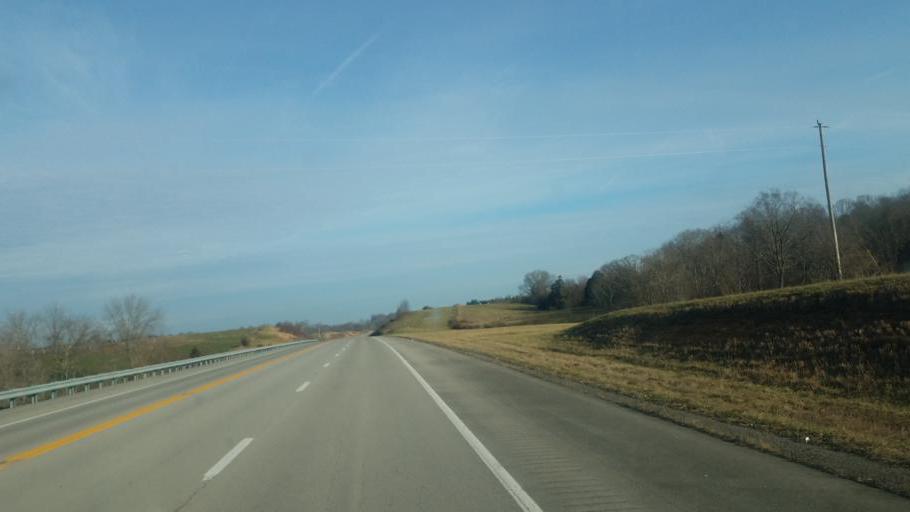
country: US
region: Kentucky
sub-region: Russell County
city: Jamestown
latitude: 36.9753
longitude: -85.0865
